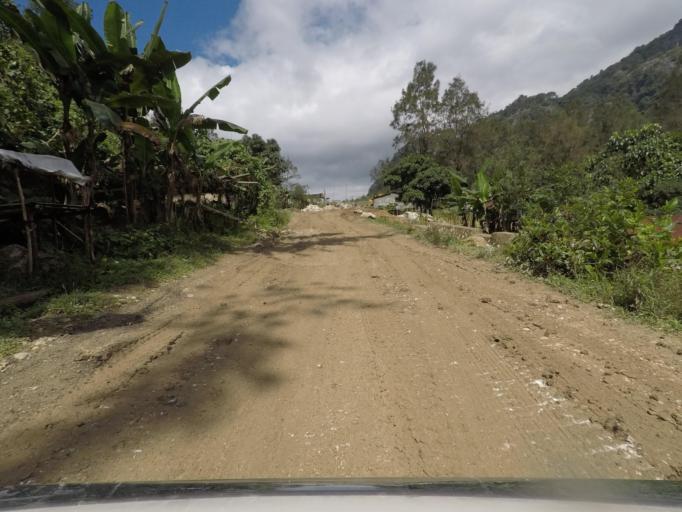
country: TL
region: Baucau
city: Venilale
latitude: -8.7258
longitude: 126.3692
